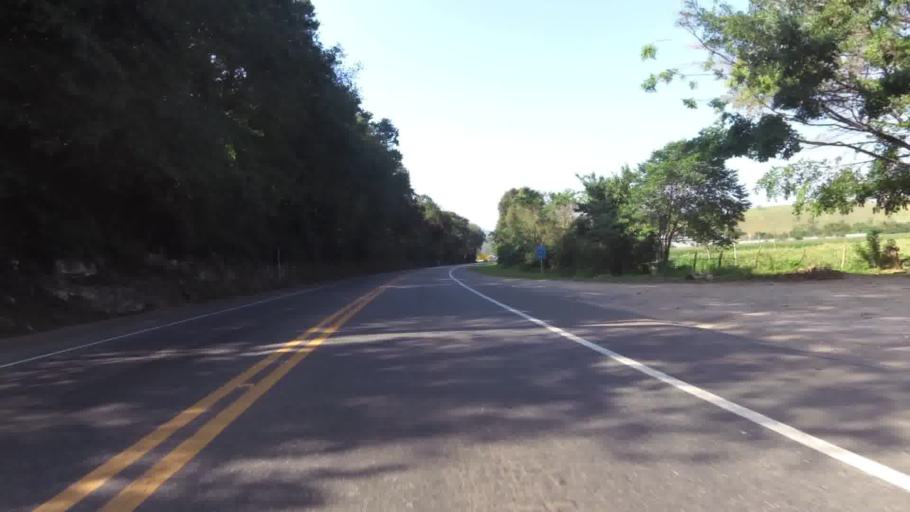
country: BR
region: Espirito Santo
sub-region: Iconha
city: Iconha
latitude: -20.8125
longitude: -40.8397
